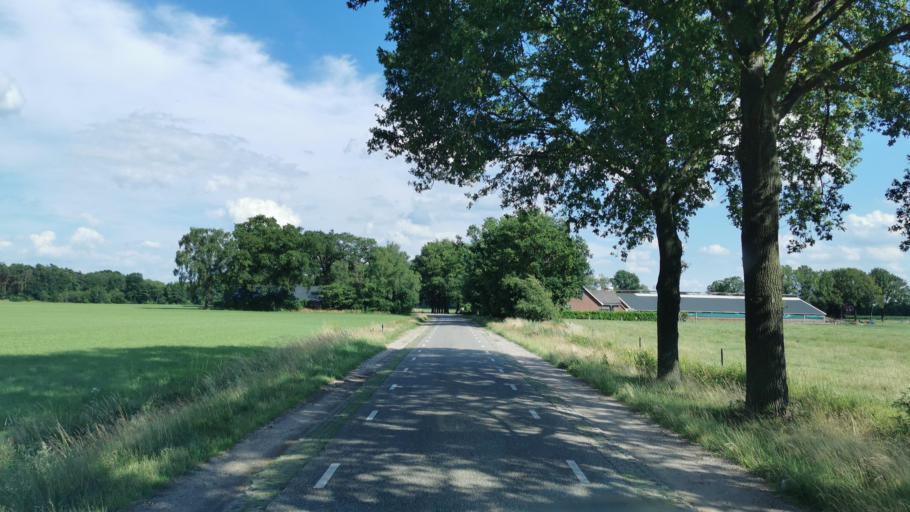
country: DE
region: Lower Saxony
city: Lage
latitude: 52.4185
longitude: 7.0057
